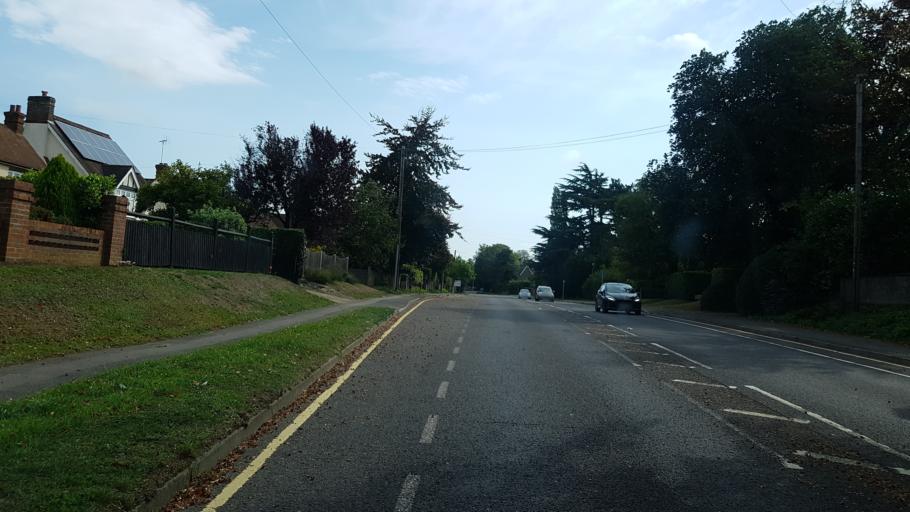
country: GB
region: England
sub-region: Kent
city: West Malling
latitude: 51.2996
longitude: 0.4078
